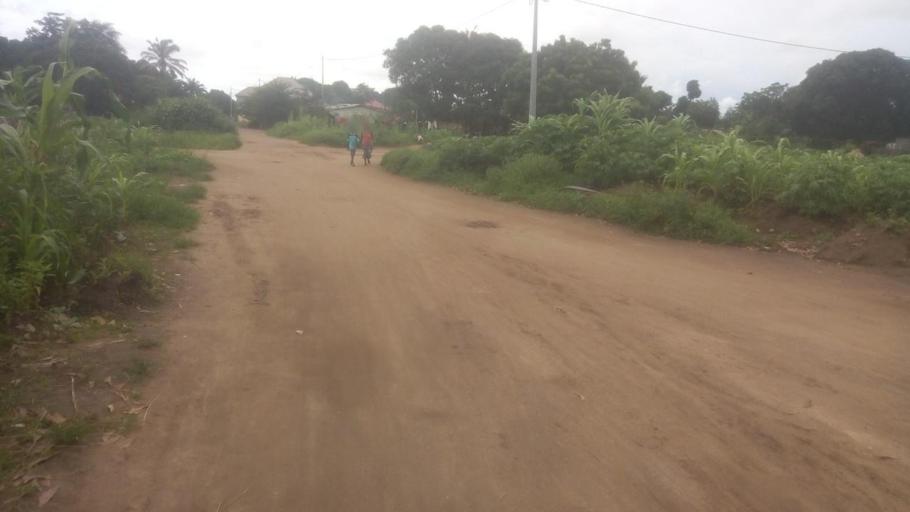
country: SL
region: Northern Province
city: Masoyila
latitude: 8.6055
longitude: -13.1865
